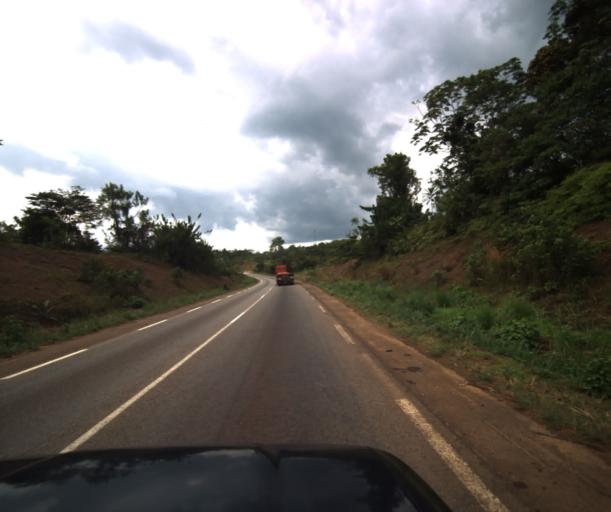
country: CM
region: Littoral
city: Edea
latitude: 3.8937
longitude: 10.0657
